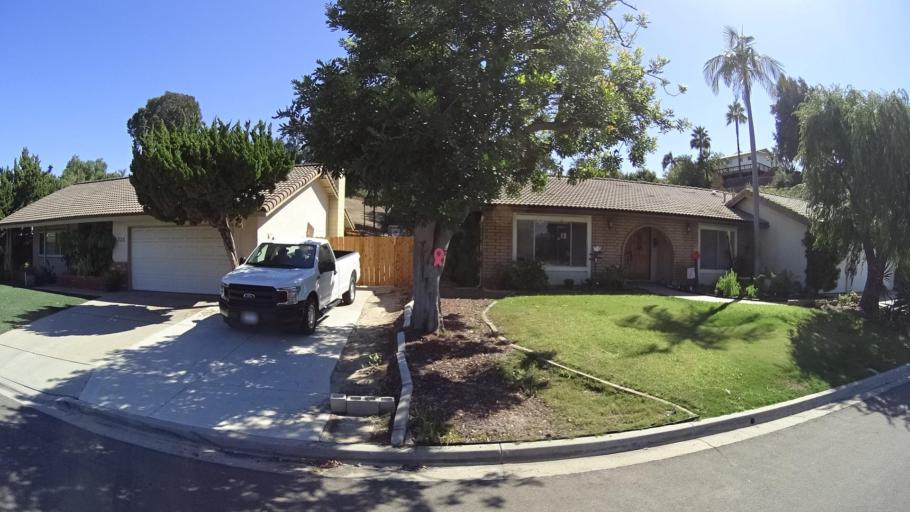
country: US
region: California
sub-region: San Diego County
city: Bonita
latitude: 32.6708
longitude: -117.0074
